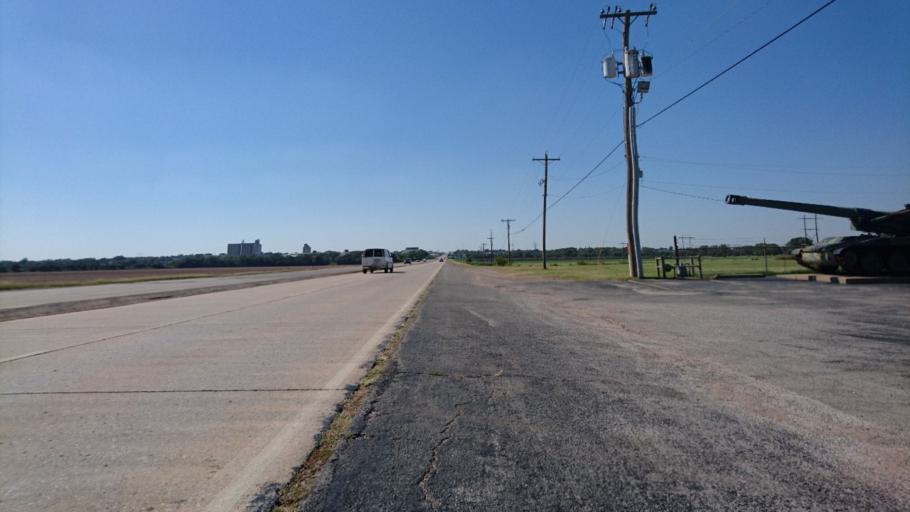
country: US
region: Oklahoma
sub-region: Custer County
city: Clinton
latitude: 35.5158
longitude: -98.9458
